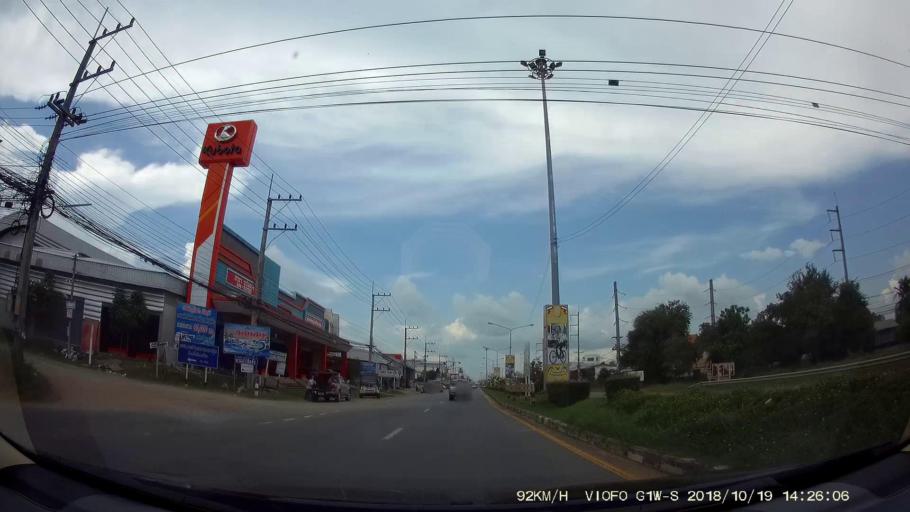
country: TH
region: Chaiyaphum
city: Kaeng Khro
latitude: 16.1029
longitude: 102.2610
